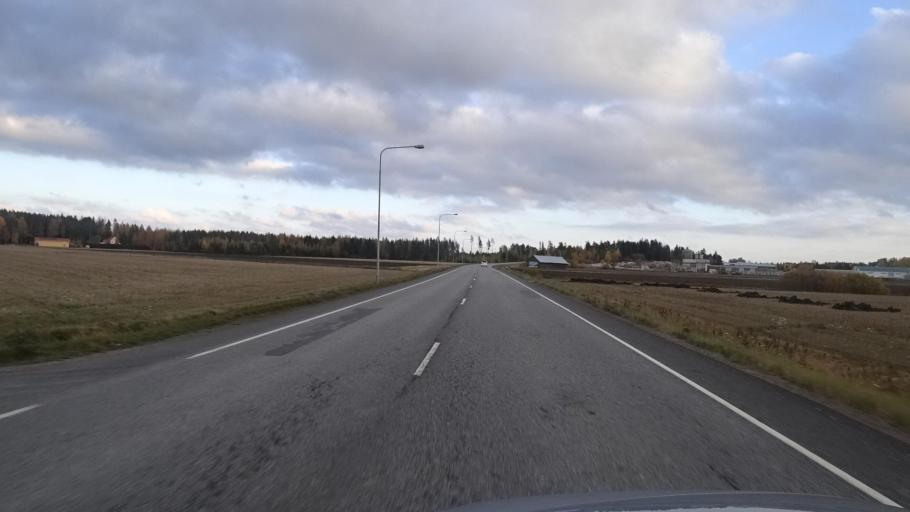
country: FI
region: Varsinais-Suomi
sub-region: Loimaa
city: Loimaa
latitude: 60.8672
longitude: 23.0096
